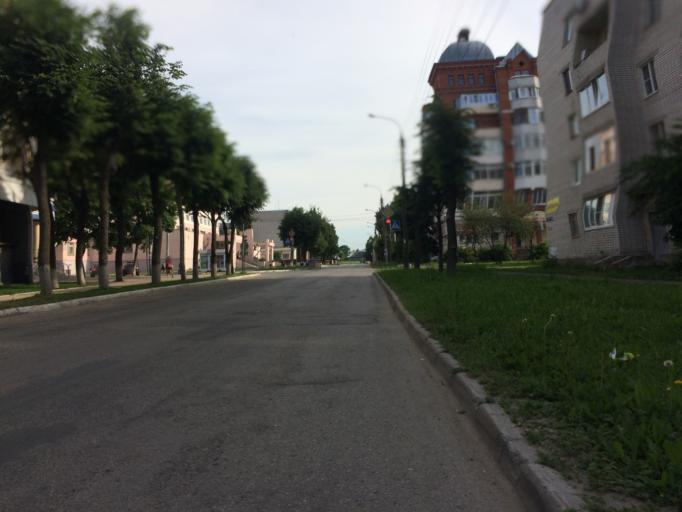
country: RU
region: Mariy-El
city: Yoshkar-Ola
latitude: 56.6429
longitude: 47.9031
